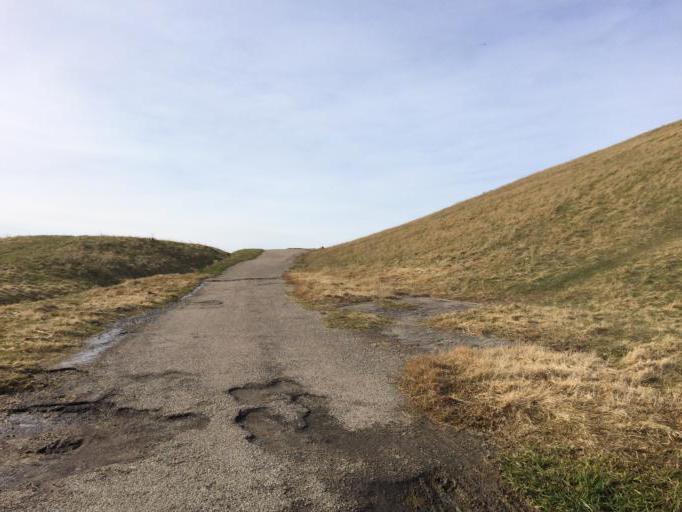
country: DK
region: Capital Region
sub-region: Albertslund Kommune
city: Albertslund
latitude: 55.6885
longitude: 12.3643
